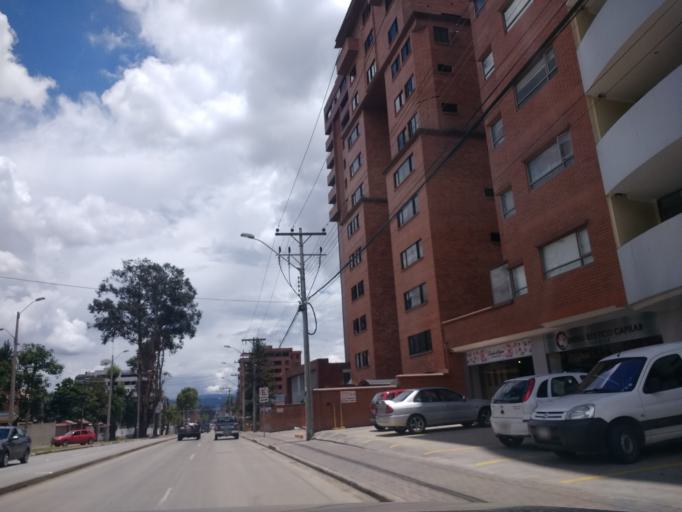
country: EC
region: Azuay
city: Cuenca
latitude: -2.8904
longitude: -79.0287
